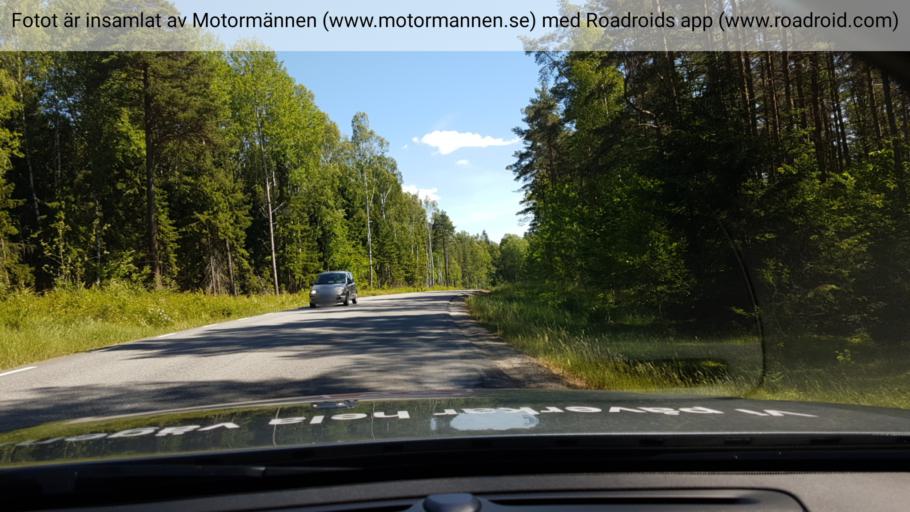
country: SE
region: Stockholm
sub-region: Haninge Kommun
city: Haninge
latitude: 59.1650
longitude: 18.1742
